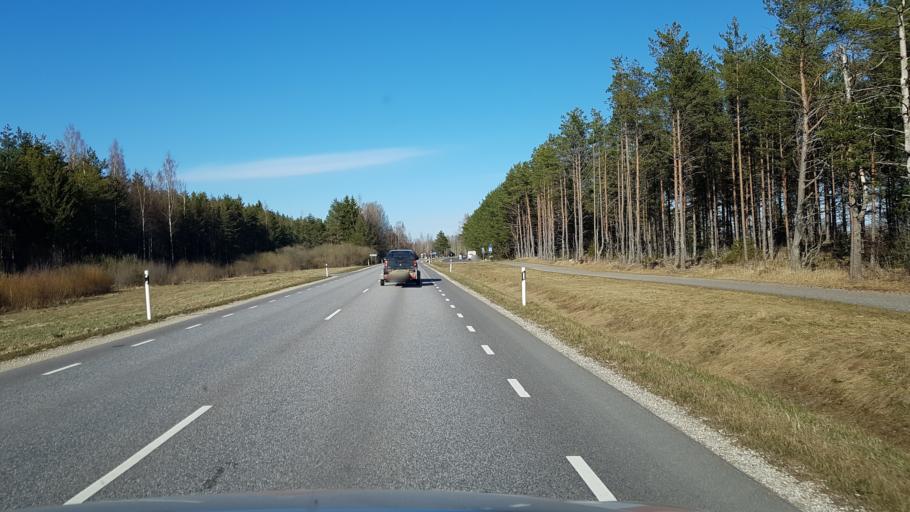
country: EE
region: Jogevamaa
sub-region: Mustvee linn
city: Mustvee
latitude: 58.9285
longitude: 27.0202
